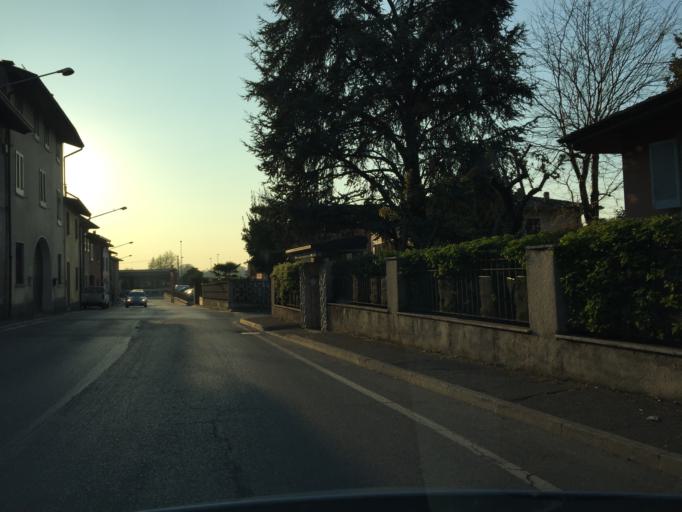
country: IT
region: Lombardy
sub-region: Provincia di Brescia
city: Pralboino
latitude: 45.2702
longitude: 10.2189
